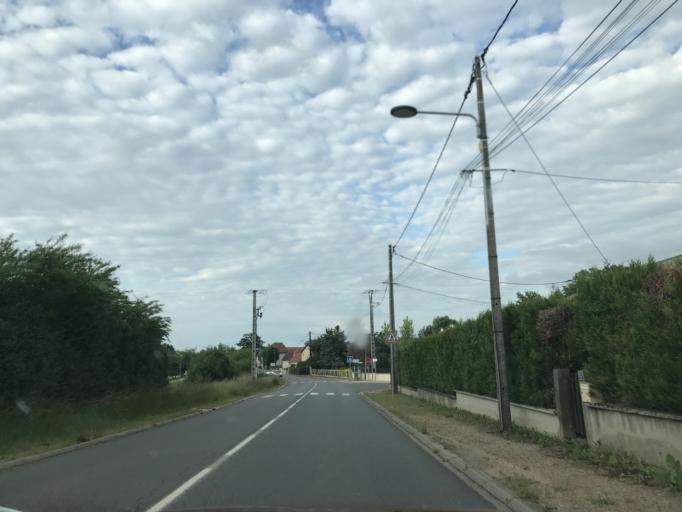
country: FR
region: Auvergne
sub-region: Departement de l'Allier
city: Bellerive-sur-Allier
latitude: 46.0969
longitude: 3.4002
